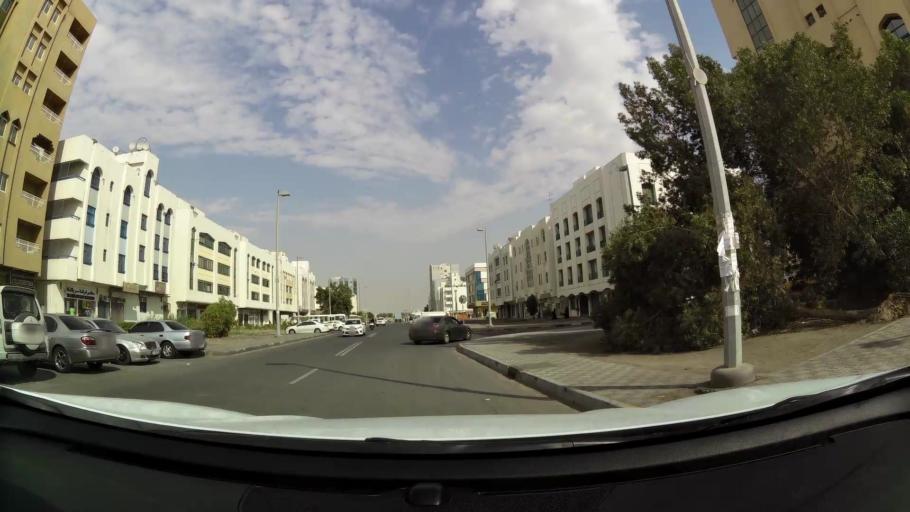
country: AE
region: Abu Dhabi
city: Abu Dhabi
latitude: 24.3311
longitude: 54.5331
